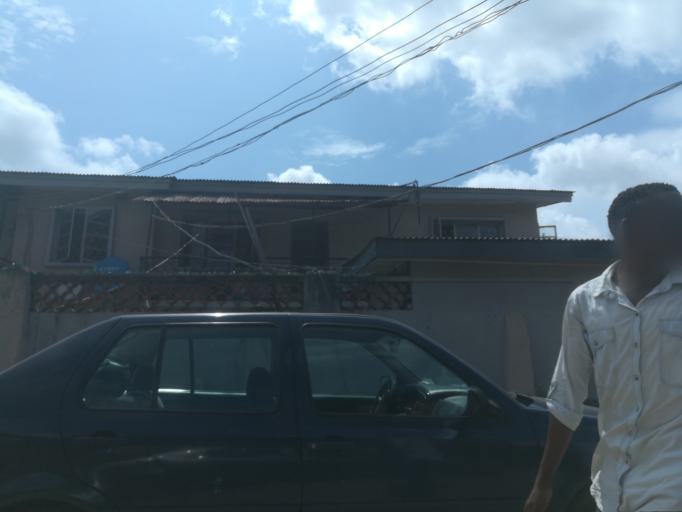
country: NG
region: Lagos
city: Somolu
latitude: 6.5276
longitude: 3.3802
